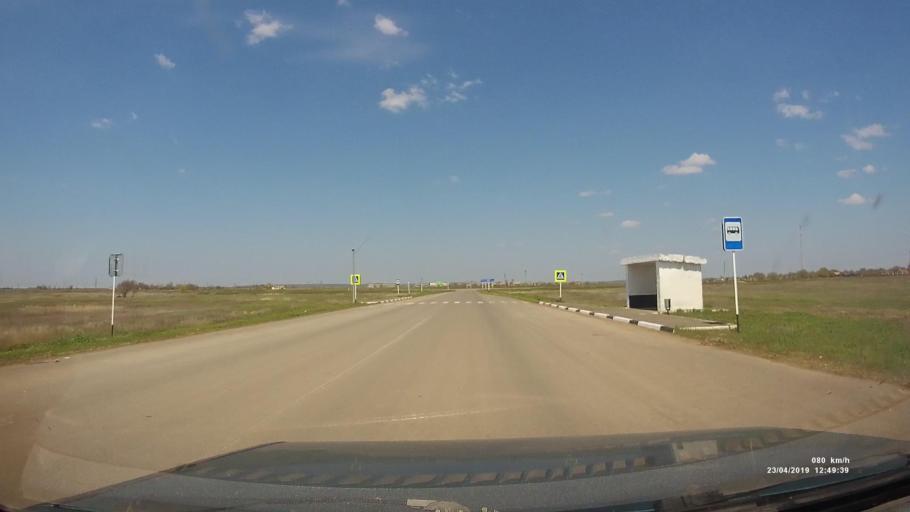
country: RU
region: Kalmykiya
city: Yashalta
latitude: 46.5399
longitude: 42.6402
